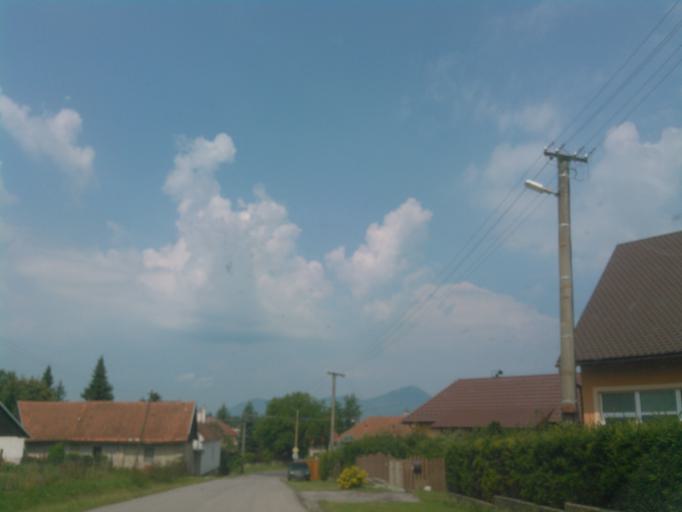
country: SK
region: Zilinsky
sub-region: Okres Liptovsky Mikulas
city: Liptovsky Mikulas
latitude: 49.0494
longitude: 19.4848
